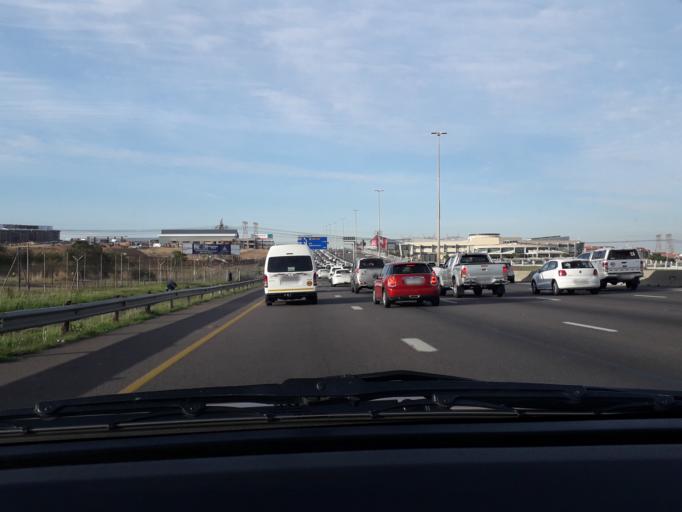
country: ZA
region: Gauteng
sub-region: City of Tshwane Metropolitan Municipality
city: Centurion
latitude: -25.9138
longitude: 28.1547
